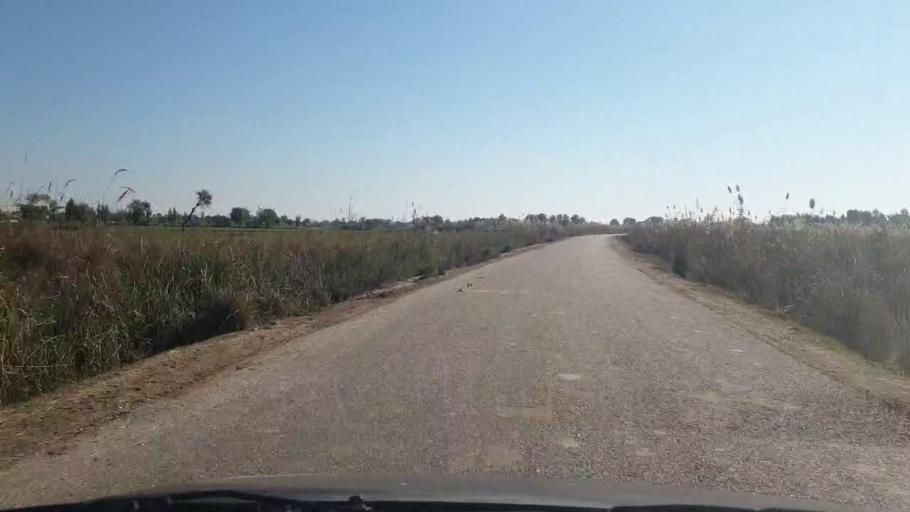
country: PK
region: Sindh
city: Bozdar
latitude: 27.1576
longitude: 68.6507
